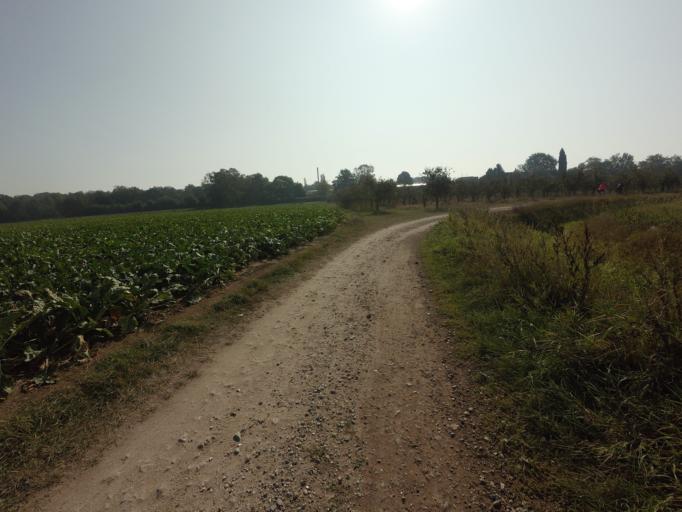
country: NL
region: Limburg
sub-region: Gemeente Beesel
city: Beesel
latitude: 51.2801
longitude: 6.0445
